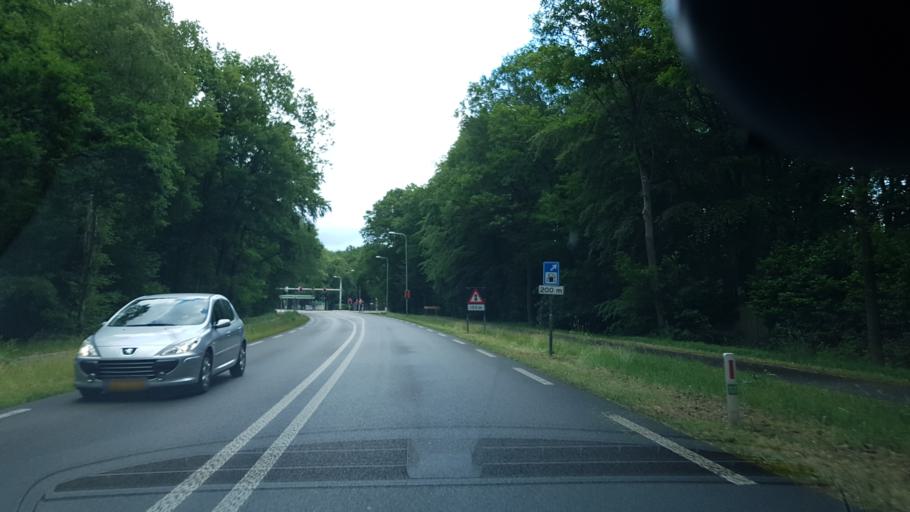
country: NL
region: Gelderland
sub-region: Gemeente Putten
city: Putten
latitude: 52.2710
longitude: 5.6143
